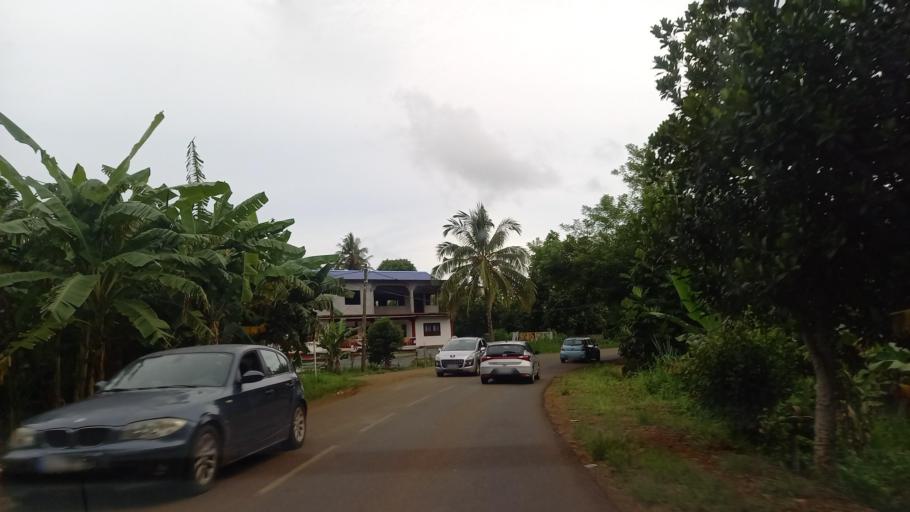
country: YT
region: Chirongui
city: Chirongui
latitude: -12.9034
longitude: 45.1504
